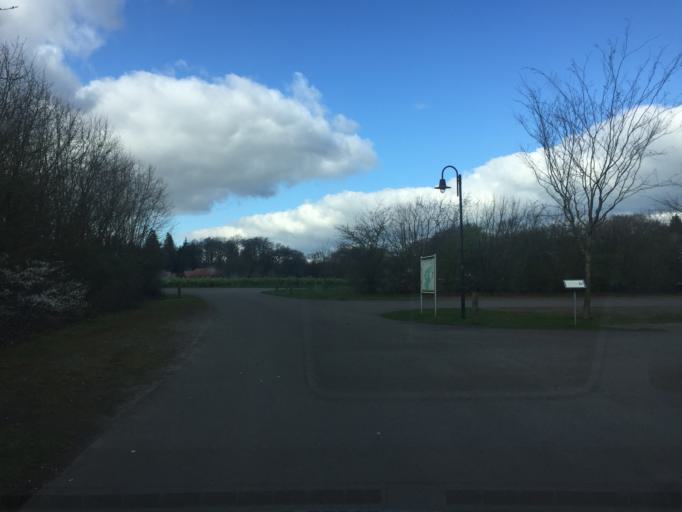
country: DE
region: Lower Saxony
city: Bruchhausen-Vilsen
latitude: 52.8028
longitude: 8.9901
